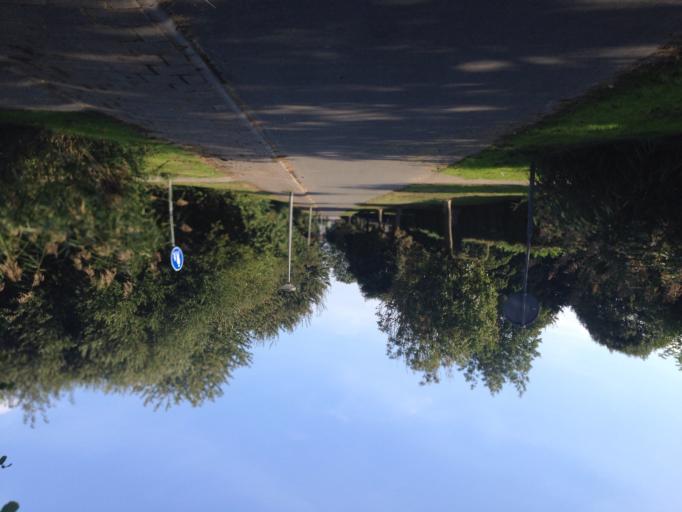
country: NL
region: Flevoland
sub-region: Gemeente Almere
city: Almere Stad
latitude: 52.3922
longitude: 5.2627
